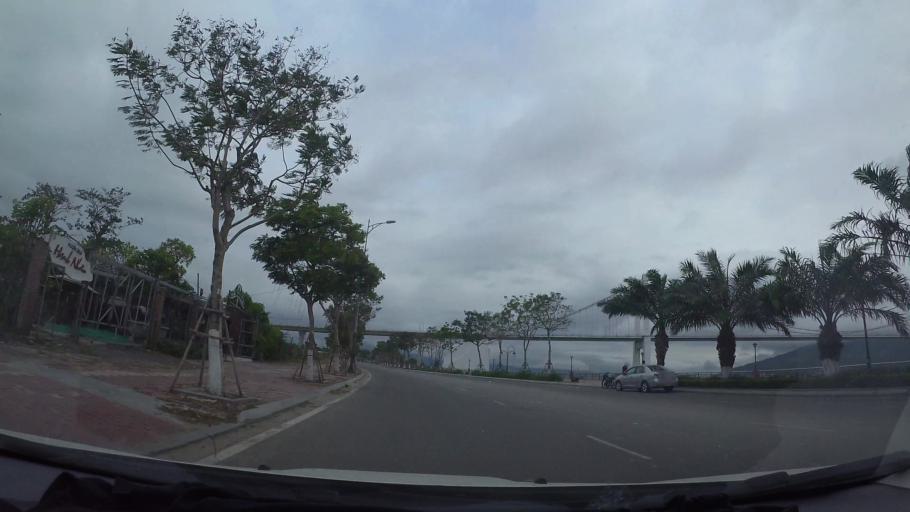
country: VN
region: Da Nang
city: Da Nang
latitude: 16.0912
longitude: 108.2191
